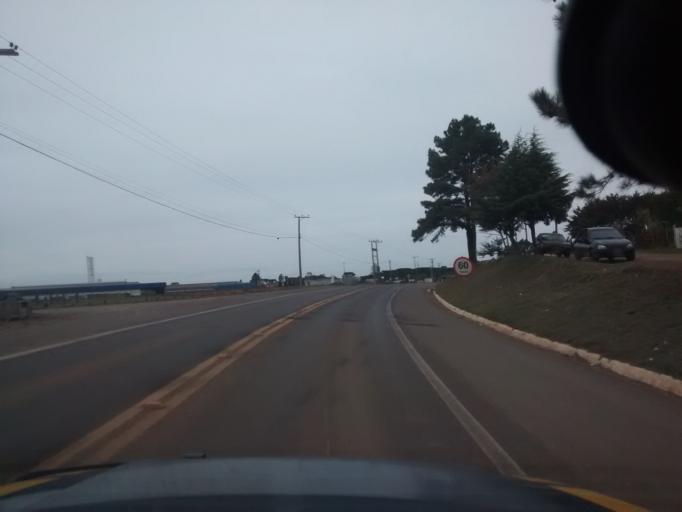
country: BR
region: Rio Grande do Sul
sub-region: Vacaria
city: Vacaria
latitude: -28.4845
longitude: -50.9601
